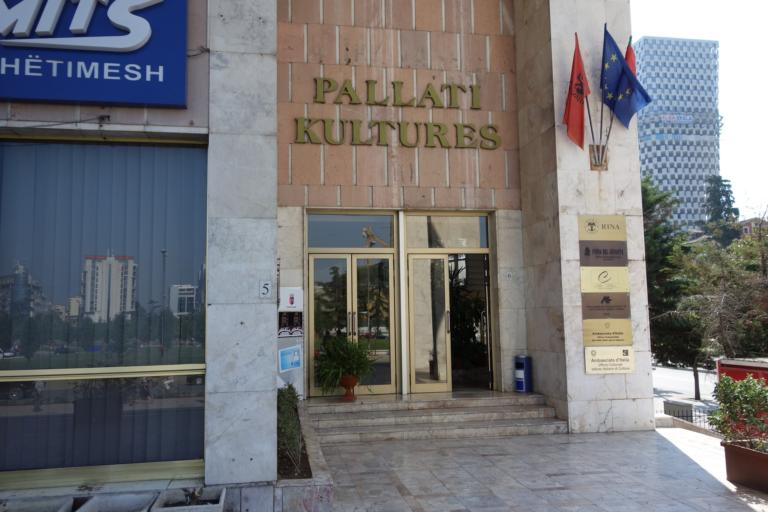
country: AL
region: Tirane
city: Tirana
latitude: 41.3283
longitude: 19.8192
